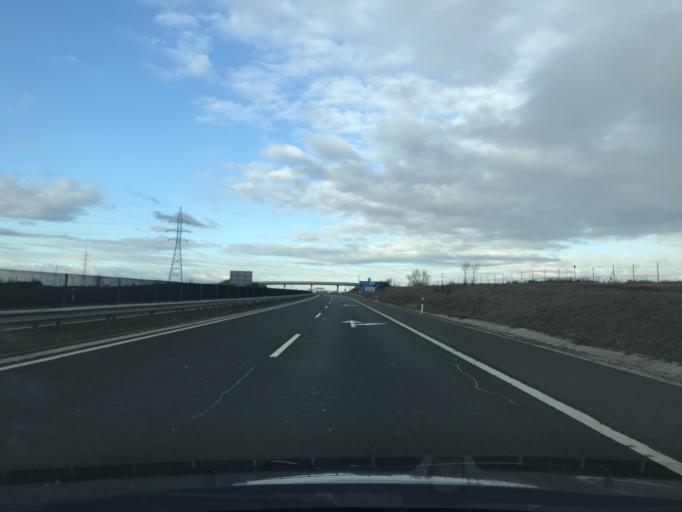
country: HU
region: Fejer
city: dunaujvaros
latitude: 46.9539
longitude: 18.8936
